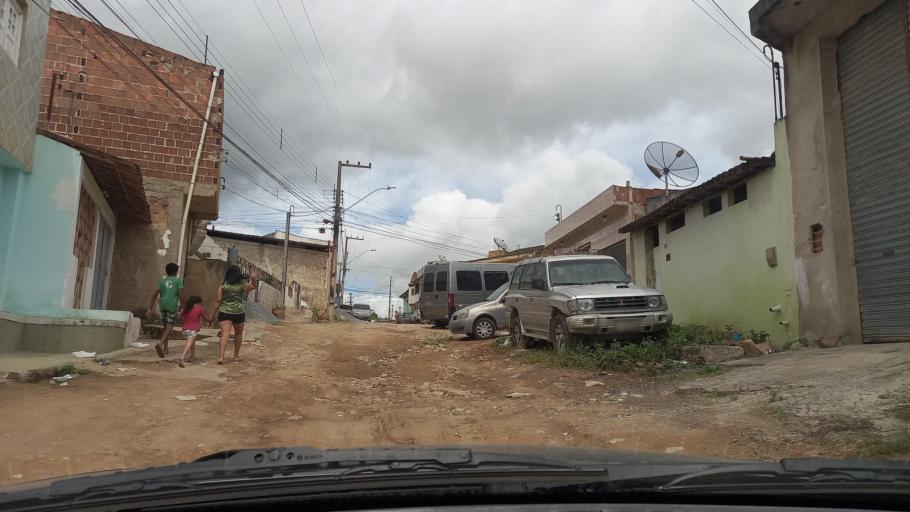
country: BR
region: Pernambuco
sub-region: Gravata
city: Gravata
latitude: -8.1959
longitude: -35.5783
